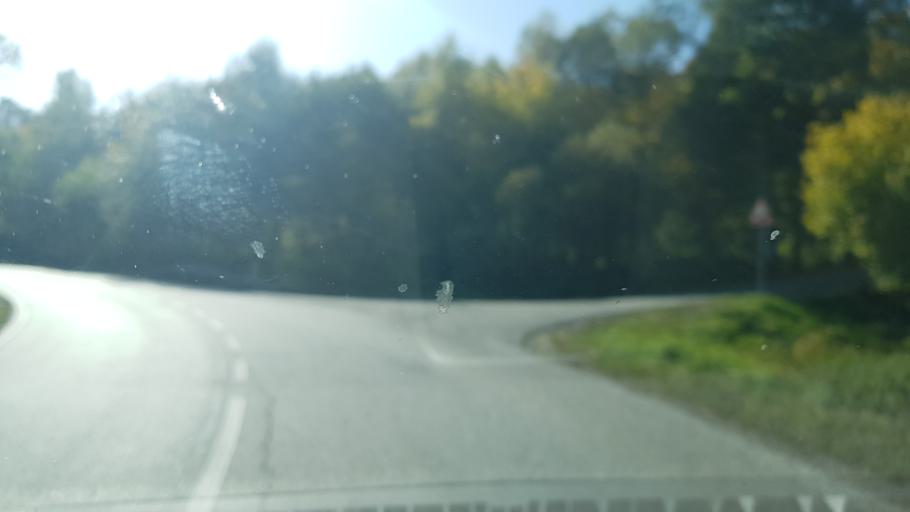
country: CZ
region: Jihocesky
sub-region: Okres Prachatice
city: Vimperk
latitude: 49.0854
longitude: 13.7869
